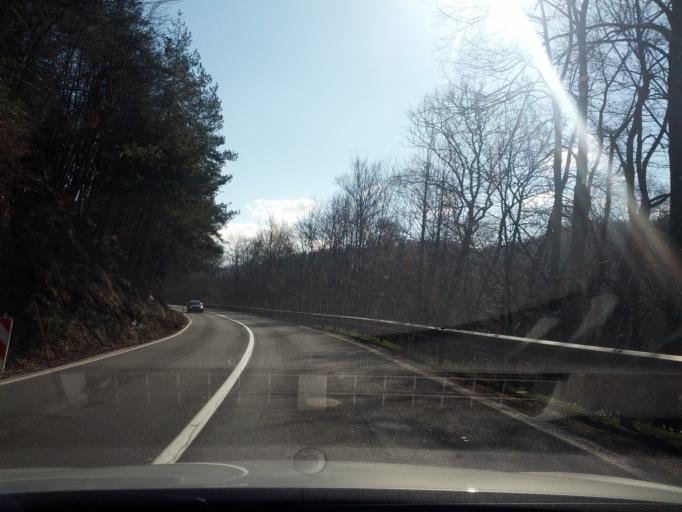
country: SI
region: Moravce
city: Moravce
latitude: 46.0919
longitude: 14.6962
